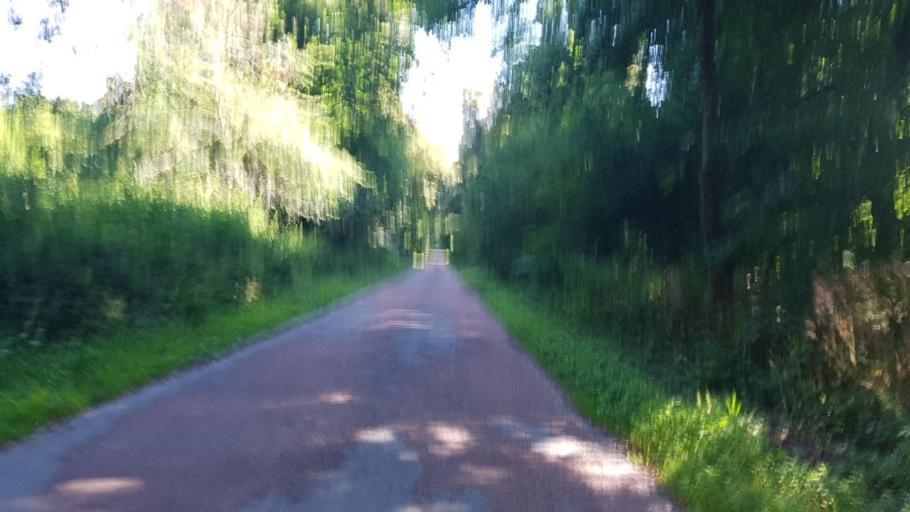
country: FR
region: Picardie
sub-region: Departement de l'Oise
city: Chamant
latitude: 49.2478
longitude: 2.6134
